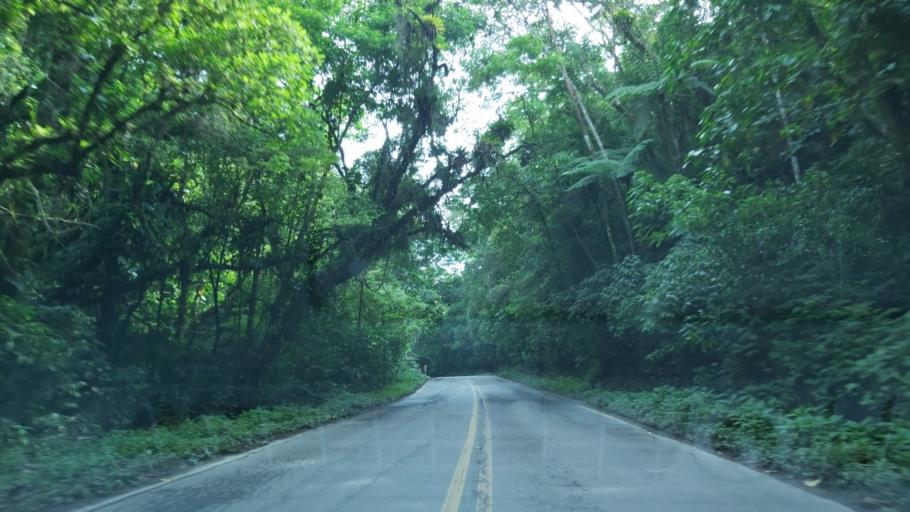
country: BR
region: Sao Paulo
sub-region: Miracatu
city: Miracatu
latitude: -24.0348
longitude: -47.5629
